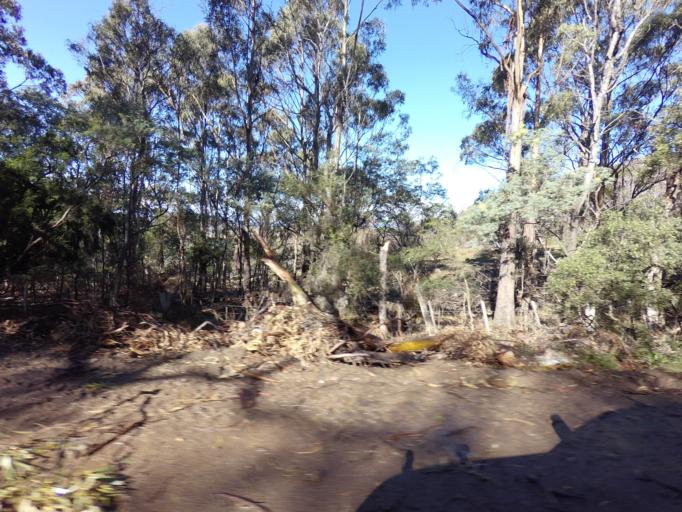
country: AU
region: Tasmania
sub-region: Sorell
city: Sorell
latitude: -42.4126
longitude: 147.9527
